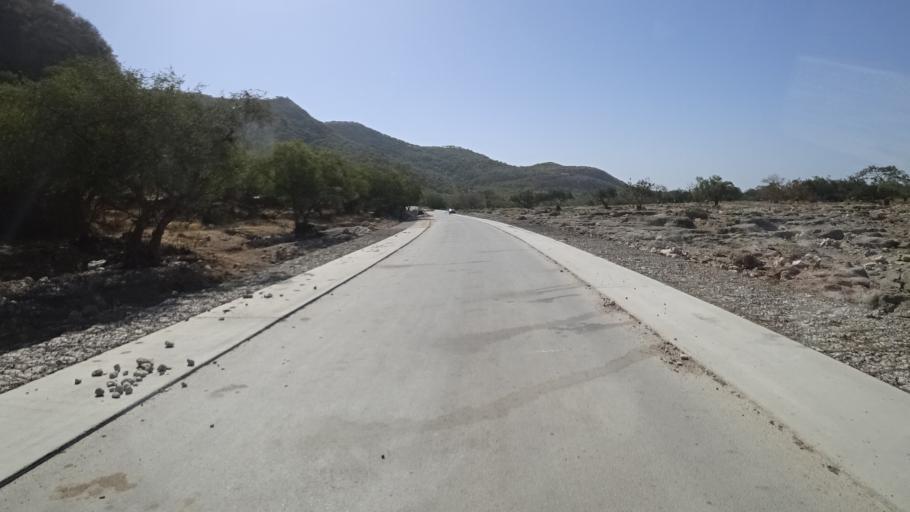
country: OM
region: Zufar
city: Salalah
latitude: 17.0846
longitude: 54.4359
